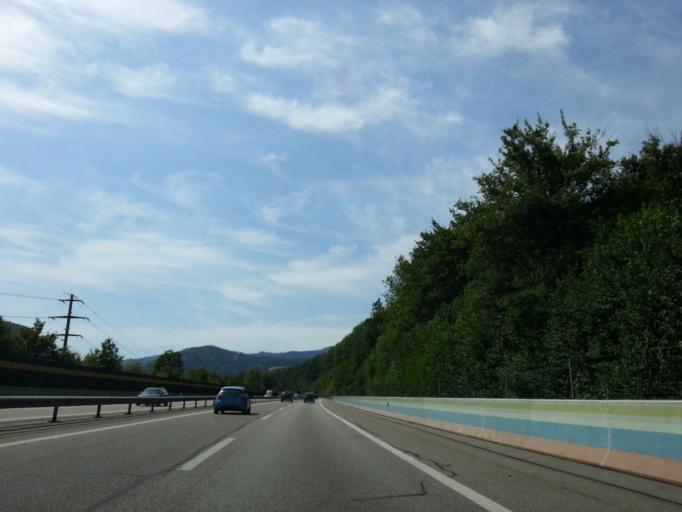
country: CH
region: Basel-Landschaft
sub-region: Bezirk Waldenburg
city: Diegten
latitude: 47.4226
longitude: 7.8094
